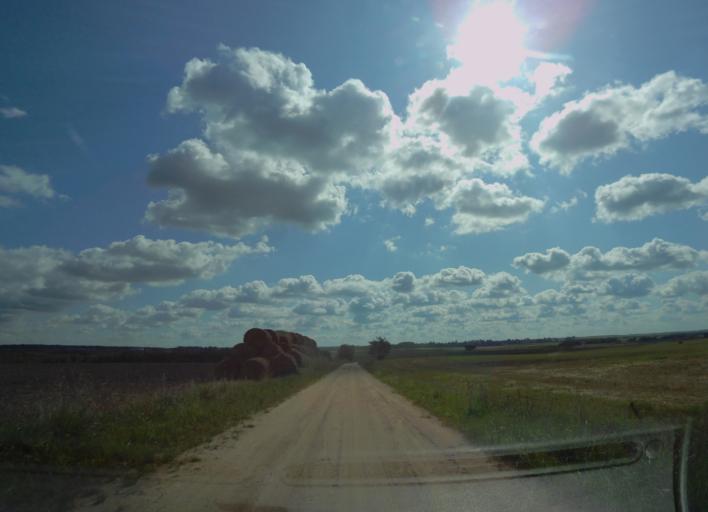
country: BY
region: Minsk
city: Zyembin
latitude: 54.3793
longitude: 28.3509
